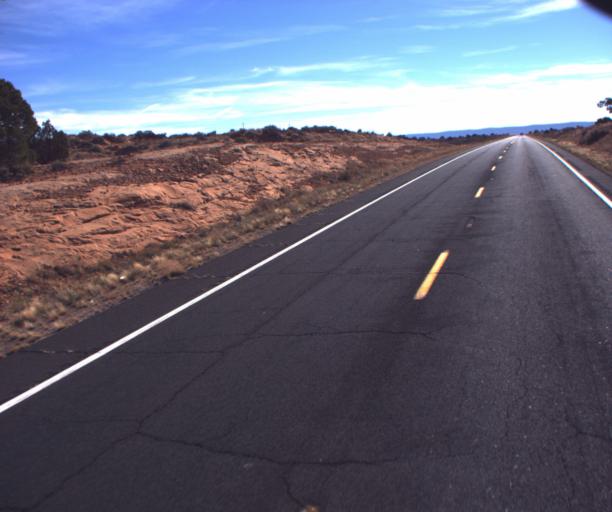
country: US
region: Arizona
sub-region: Coconino County
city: Kaibito
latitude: 36.5719
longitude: -110.7663
